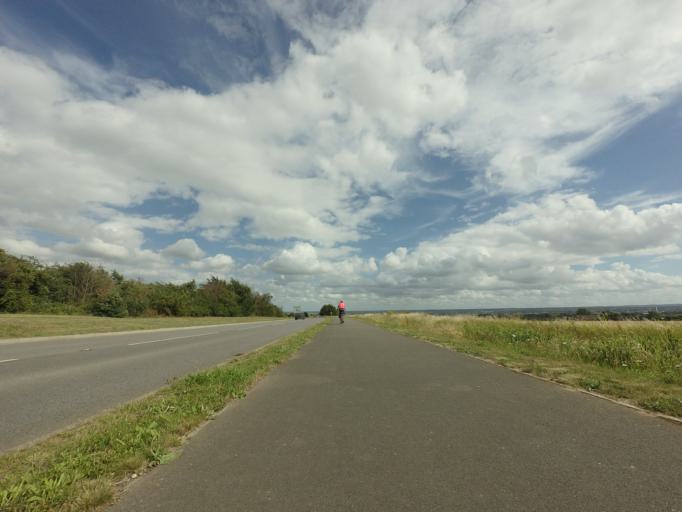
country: GB
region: England
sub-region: Kent
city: Hoo
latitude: 51.4292
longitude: 0.5747
